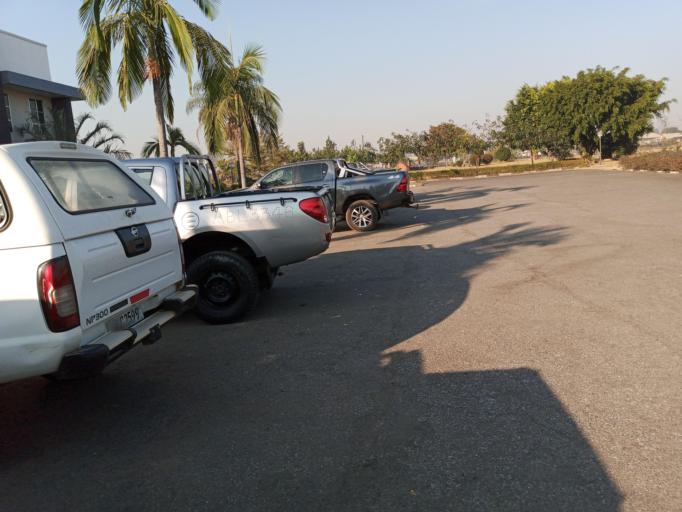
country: ZM
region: Copperbelt
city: Kitwe
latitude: -12.8745
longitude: 28.2536
